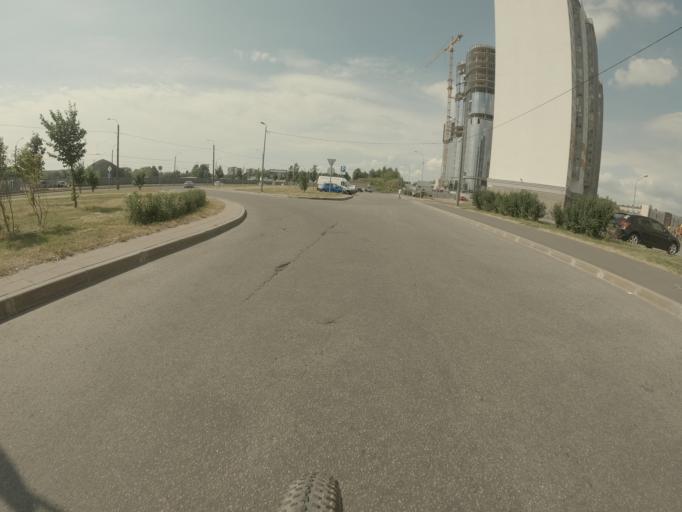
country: RU
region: St.-Petersburg
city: Centralniy
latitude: 59.9167
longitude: 30.4305
